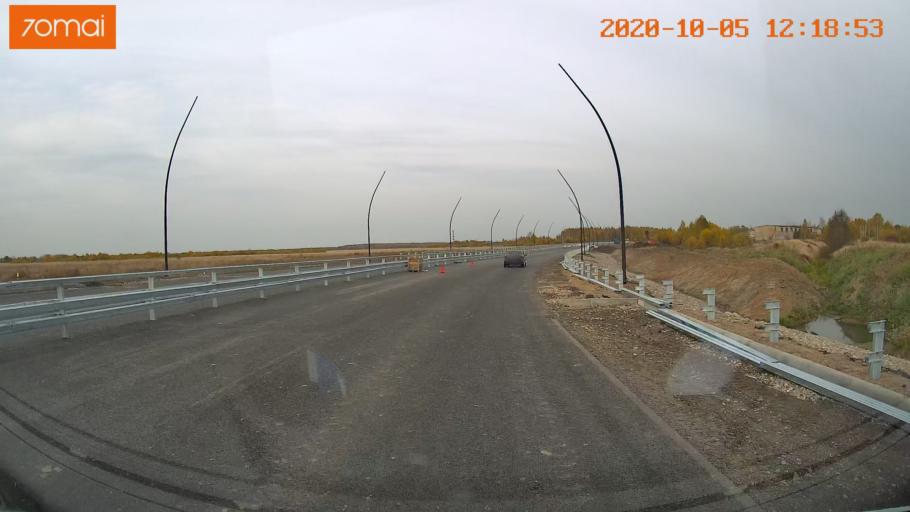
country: RU
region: Ivanovo
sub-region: Gorod Ivanovo
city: Ivanovo
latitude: 56.9515
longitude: 40.9380
